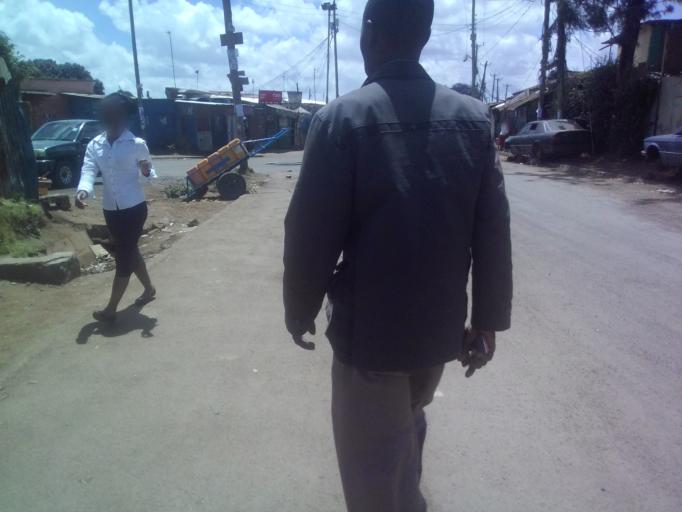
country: KE
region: Nairobi Area
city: Nairobi
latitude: -1.3073
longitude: 36.7775
